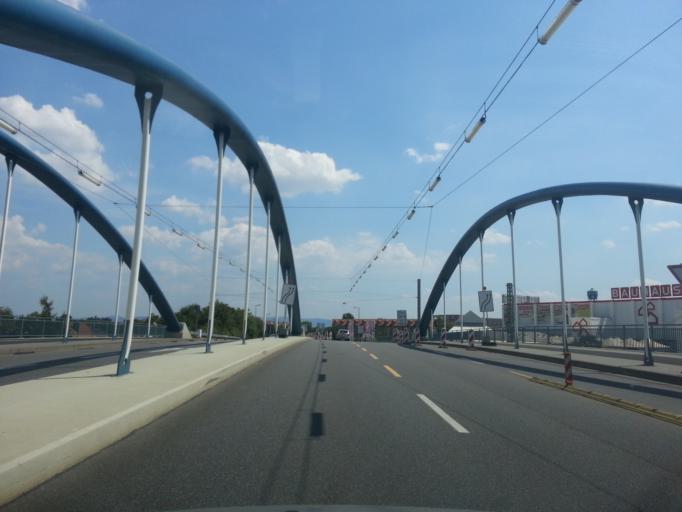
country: DE
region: Baden-Wuerttemberg
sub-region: Karlsruhe Region
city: Mannheim
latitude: 49.5315
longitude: 8.4819
